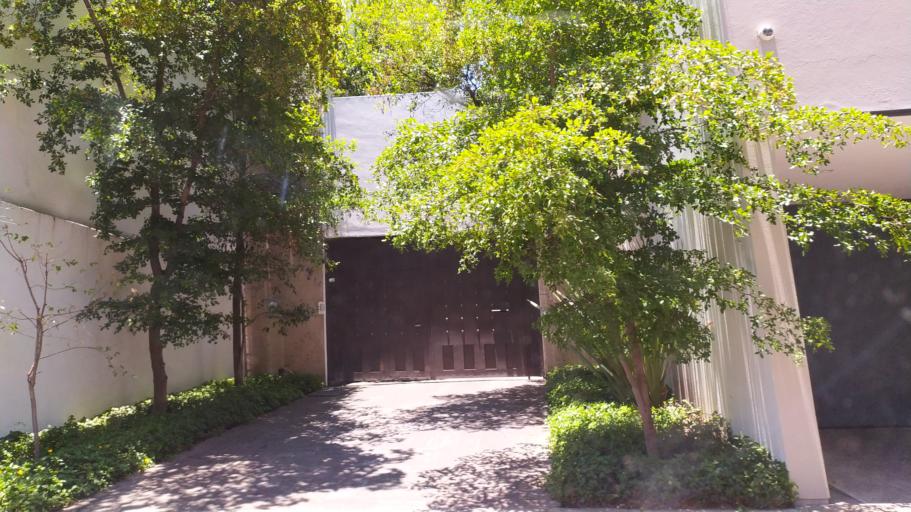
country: MX
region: Jalisco
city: Guadalajara
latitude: 20.6868
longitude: -103.4020
